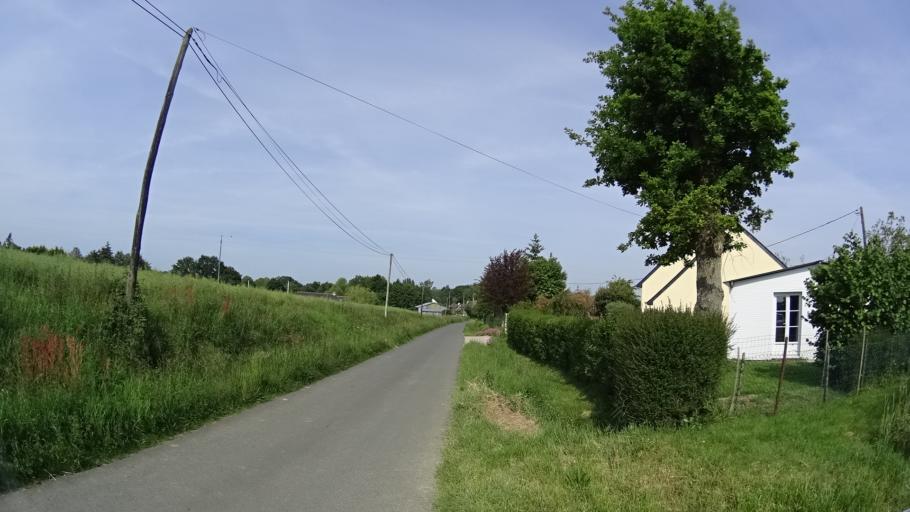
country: FR
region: Brittany
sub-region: Departement d'Ille-et-Vilaine
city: Nouvoitou
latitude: 48.0218
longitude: -1.5452
